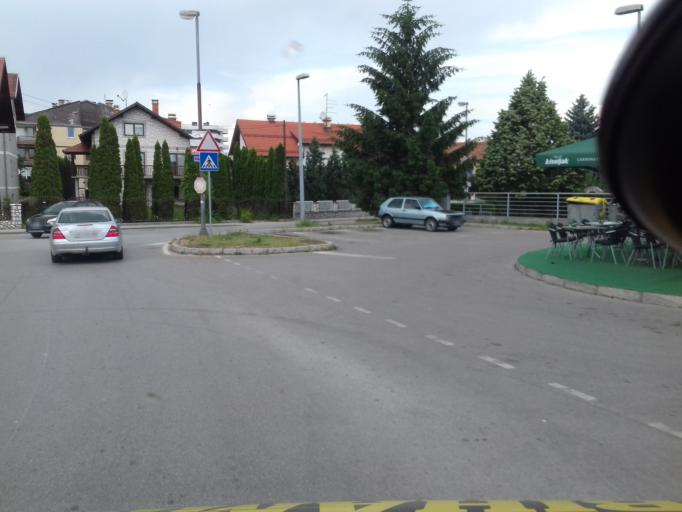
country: BA
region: Federation of Bosnia and Herzegovina
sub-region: Kanton Sarajevo
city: Sarajevo
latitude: 43.8365
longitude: 18.2990
